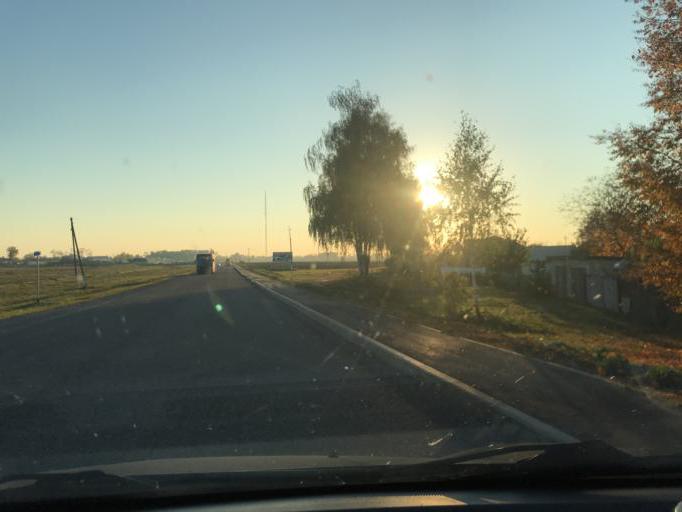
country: BY
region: Gomel
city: Brahin
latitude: 51.8076
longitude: 30.2799
